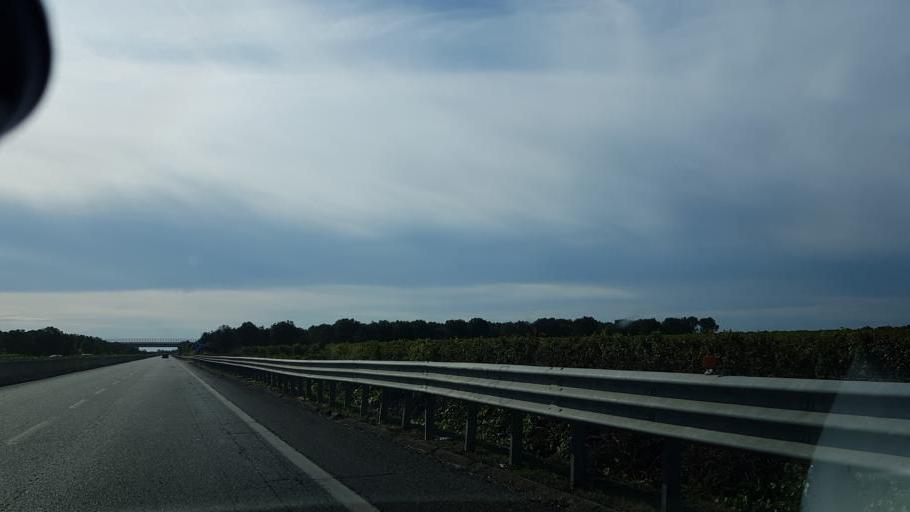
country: IT
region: Apulia
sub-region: Provincia di Brindisi
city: San Pietro Vernotico
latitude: 40.5394
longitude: 18.0037
